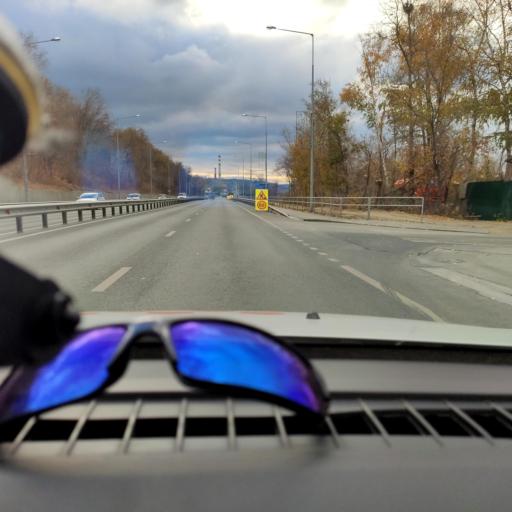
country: RU
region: Samara
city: Volzhskiy
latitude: 53.3898
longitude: 50.1591
